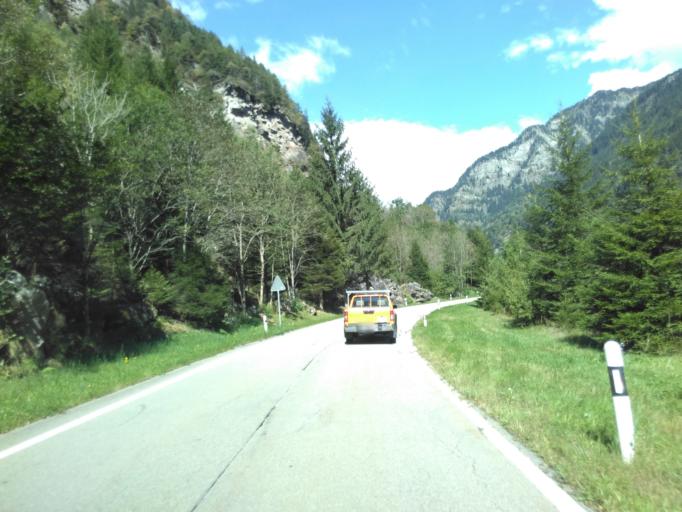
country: CH
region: Grisons
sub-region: Moesa District
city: Arvigo
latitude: 46.3144
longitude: 9.1157
